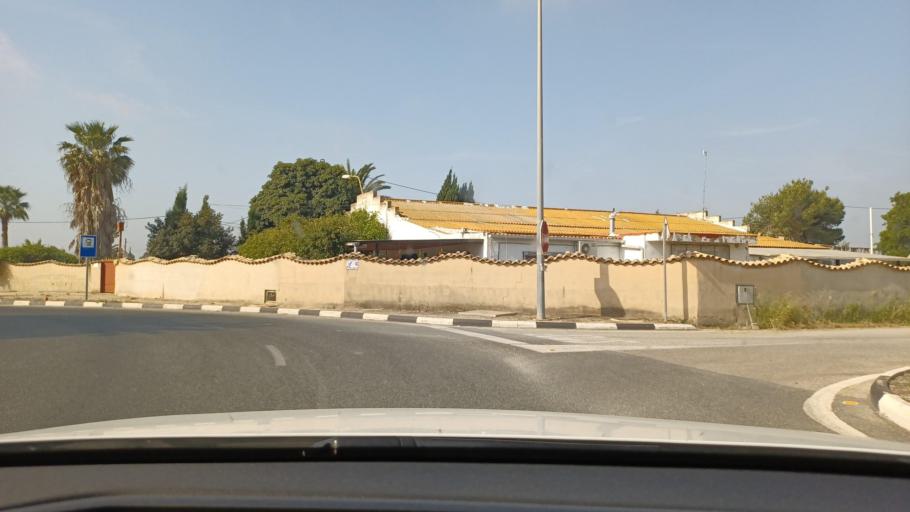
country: ES
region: Valencia
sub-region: Provincia de Alicante
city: Dolores
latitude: 38.1799
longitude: -0.7019
